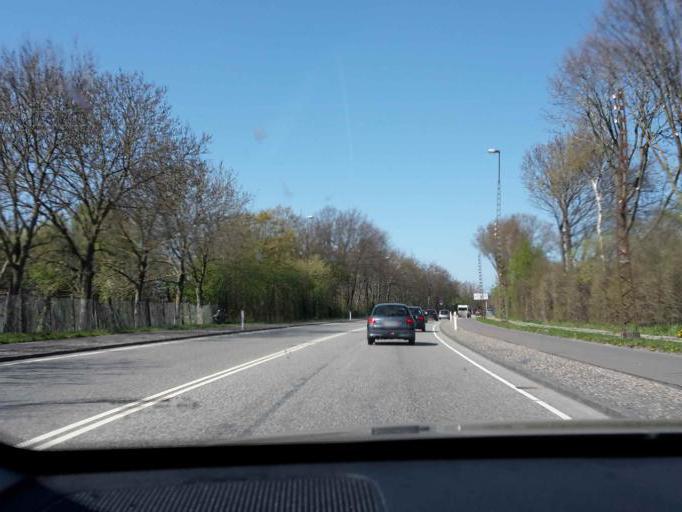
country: DK
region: South Denmark
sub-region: Odense Kommune
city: Odense
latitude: 55.3832
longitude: 10.3593
